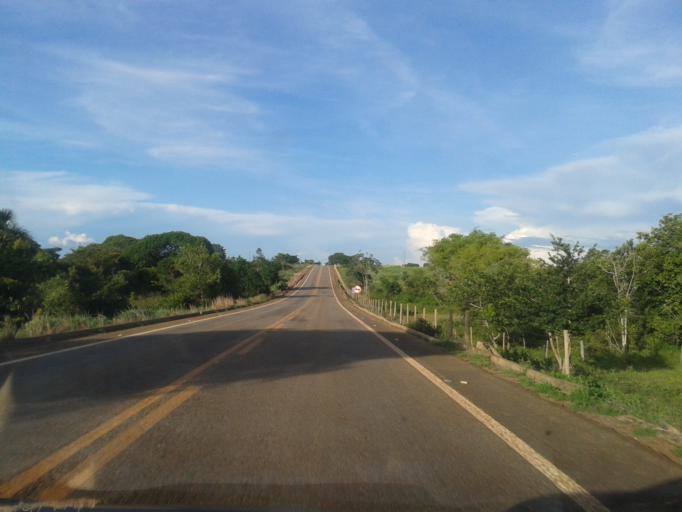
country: BR
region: Goias
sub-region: Sao Miguel Do Araguaia
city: Sao Miguel do Araguaia
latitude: -13.4392
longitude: -50.2875
